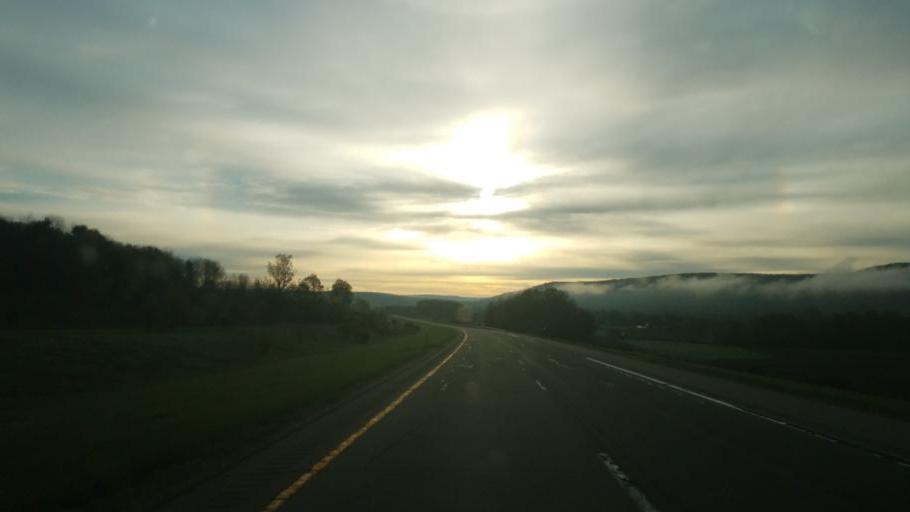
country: US
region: New York
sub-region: Allegany County
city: Friendship
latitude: 42.2199
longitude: -78.1159
